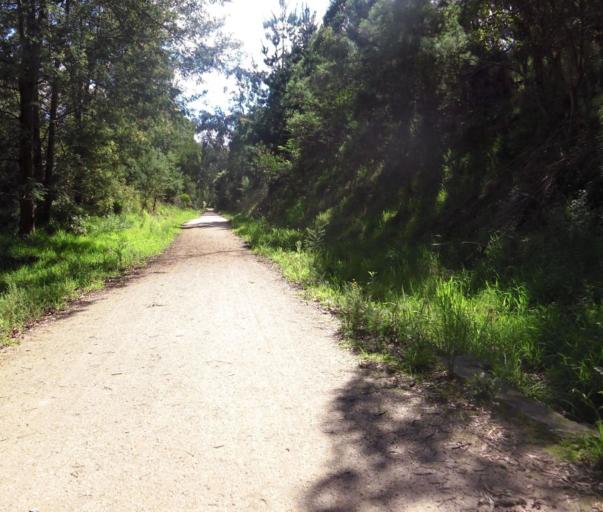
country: AU
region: Victoria
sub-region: Bass Coast
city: North Wonthaggi
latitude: -38.6911
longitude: 146.0733
